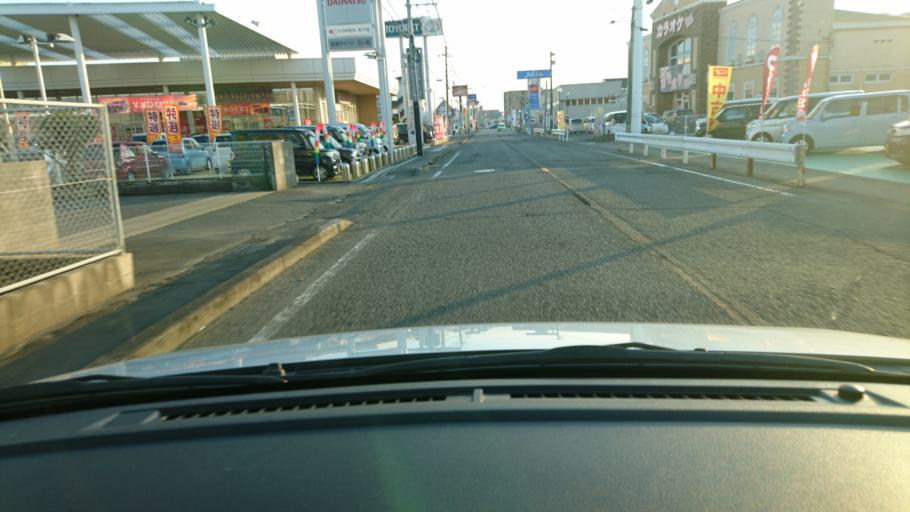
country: JP
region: Miyazaki
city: Miyazaki-shi
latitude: 31.9540
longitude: 131.4347
